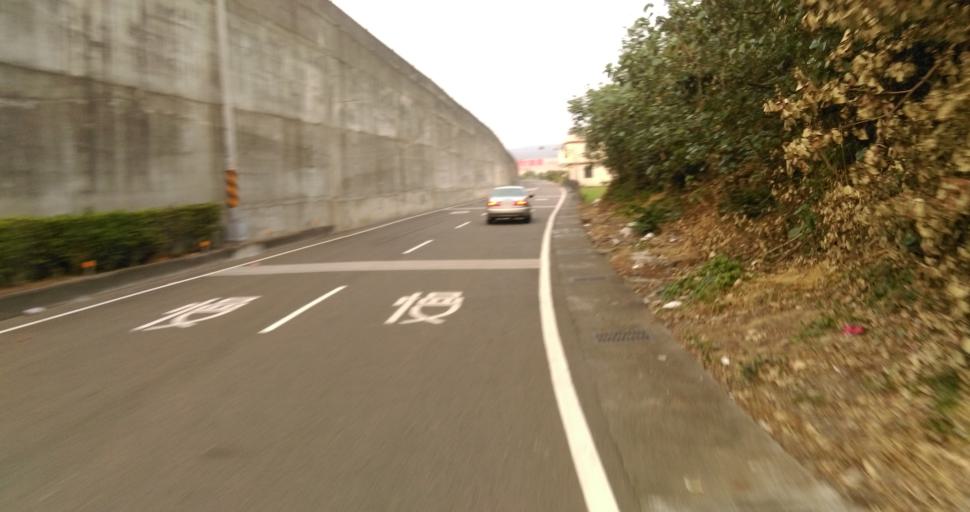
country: TW
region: Taiwan
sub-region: Hsinchu
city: Zhubei
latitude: 24.8621
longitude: 120.9519
